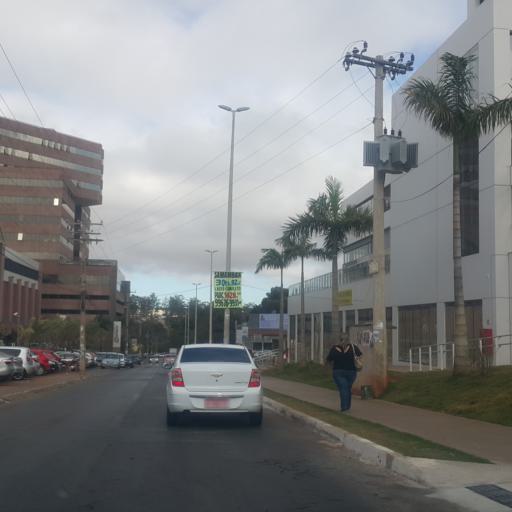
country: BR
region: Federal District
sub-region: Brasilia
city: Brasilia
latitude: -15.8230
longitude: -48.0657
